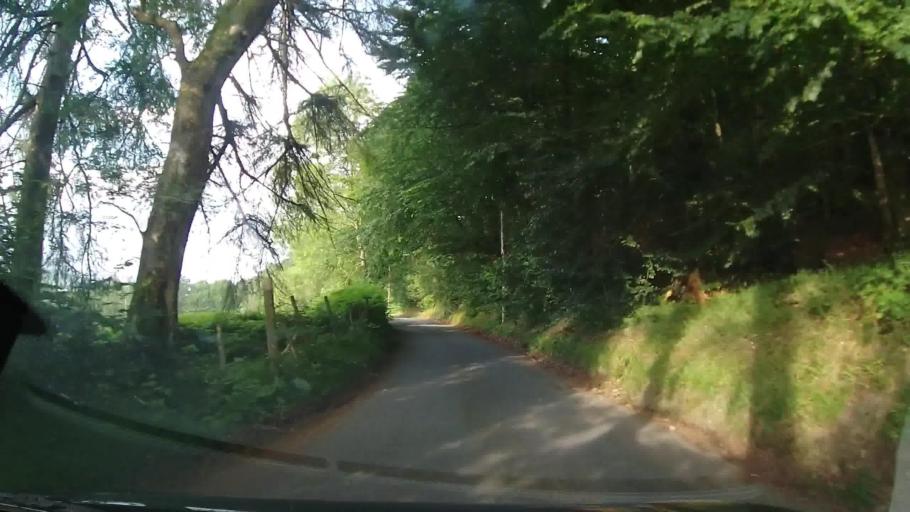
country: GB
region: Wales
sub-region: Gwynedd
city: Bala
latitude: 52.8868
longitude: -3.6155
